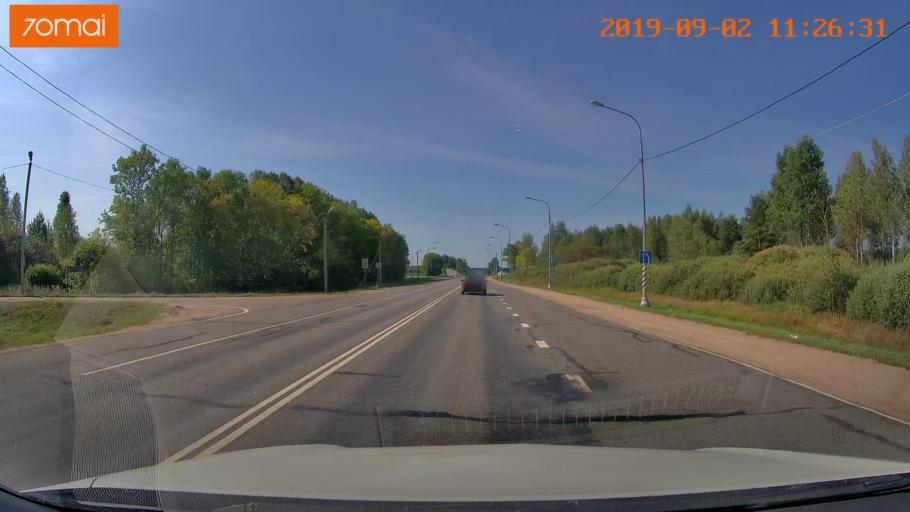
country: RU
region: Smolensk
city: Roslavl'
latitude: 53.9920
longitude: 32.9299
